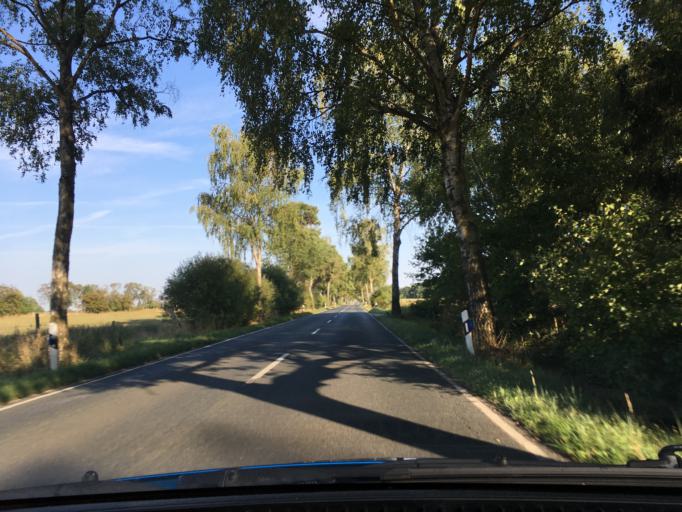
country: DE
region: Lower Saxony
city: Burgdorf
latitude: 52.4746
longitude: 9.9564
